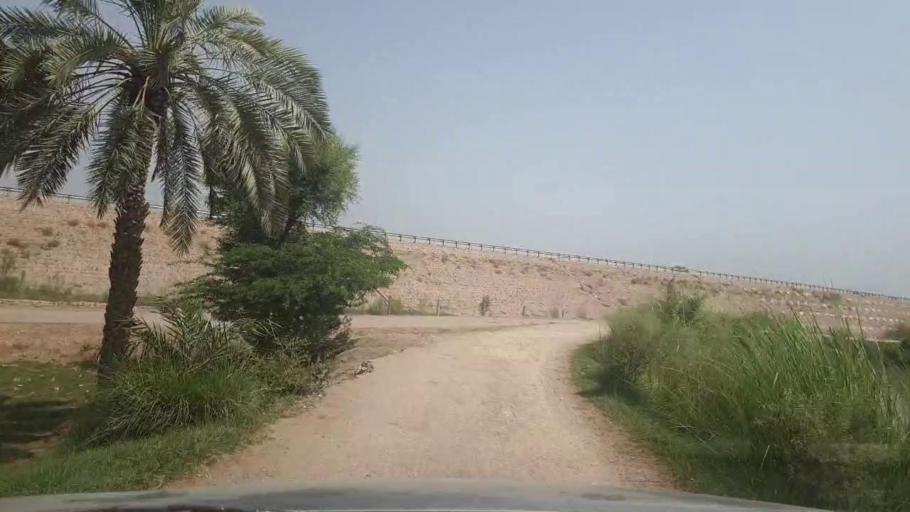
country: PK
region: Sindh
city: Pano Aqil
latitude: 27.9026
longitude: 69.1476
